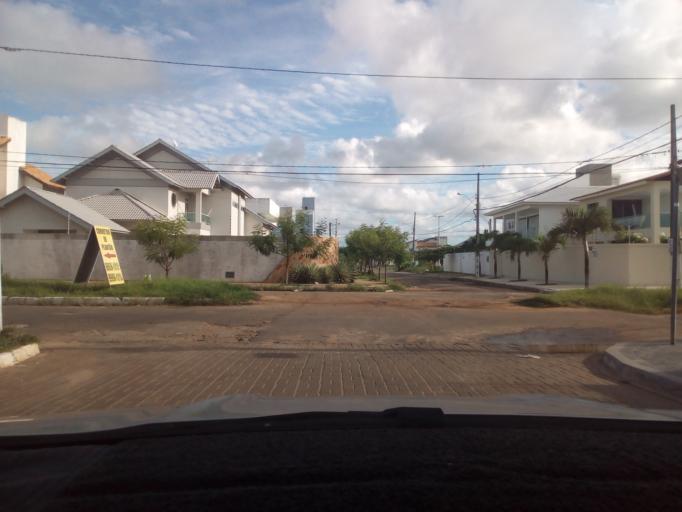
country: BR
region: Paraiba
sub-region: Joao Pessoa
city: Joao Pessoa
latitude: -7.0517
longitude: -34.8457
